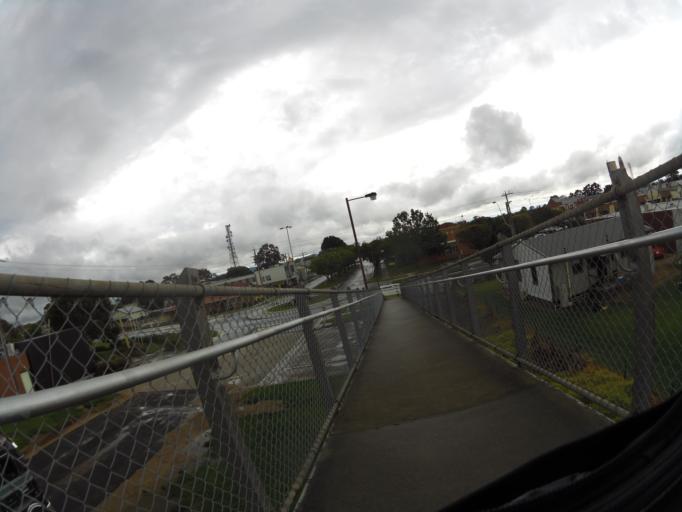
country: AU
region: Victoria
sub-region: East Gippsland
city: Bairnsdale
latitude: -37.8292
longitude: 147.6251
